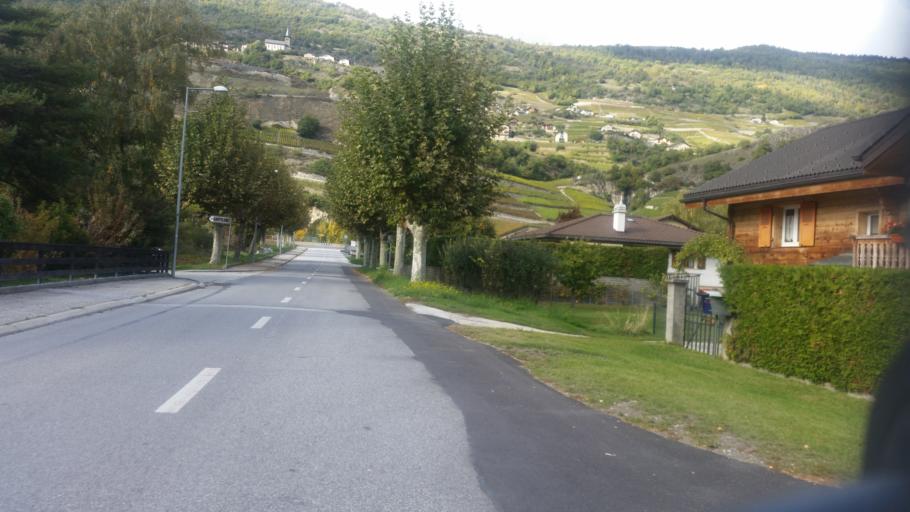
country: CH
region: Valais
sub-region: Sierre District
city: Grone
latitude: 46.2634
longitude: 7.4605
